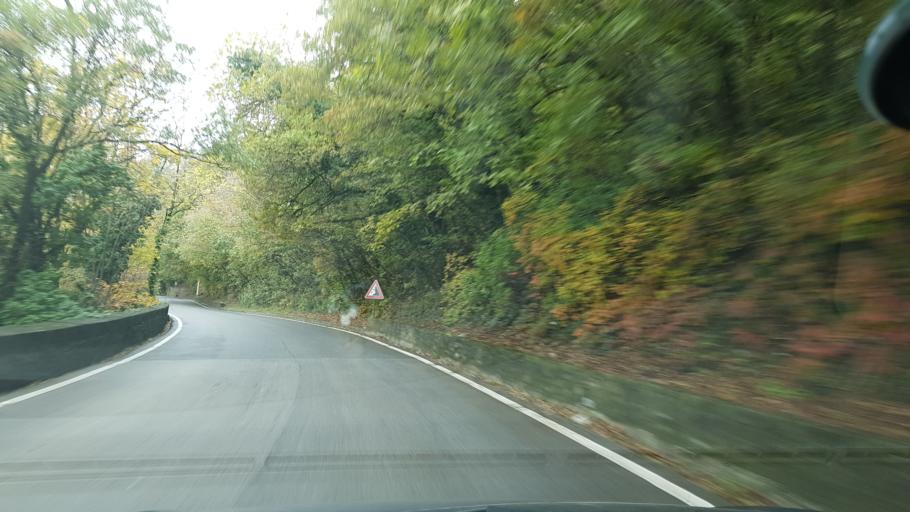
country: IT
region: Friuli Venezia Giulia
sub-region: Provincia di Trieste
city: Prosecco-Contovello
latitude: 45.6930
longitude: 13.7443
